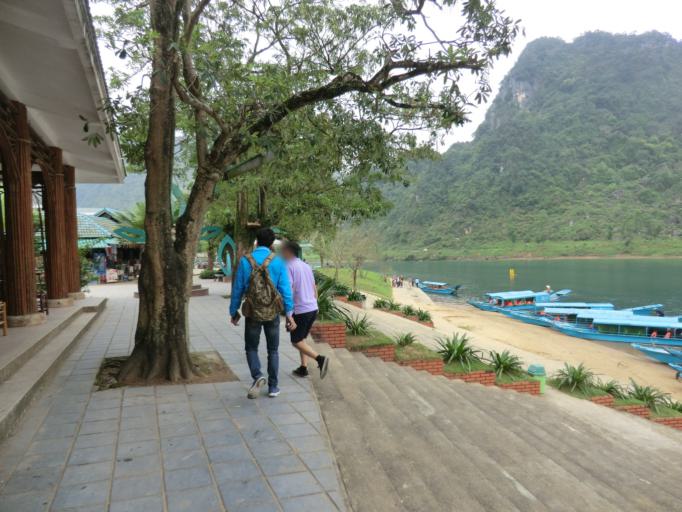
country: VN
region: Quang Binh
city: Ba Don
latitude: 17.6125
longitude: 106.3062
